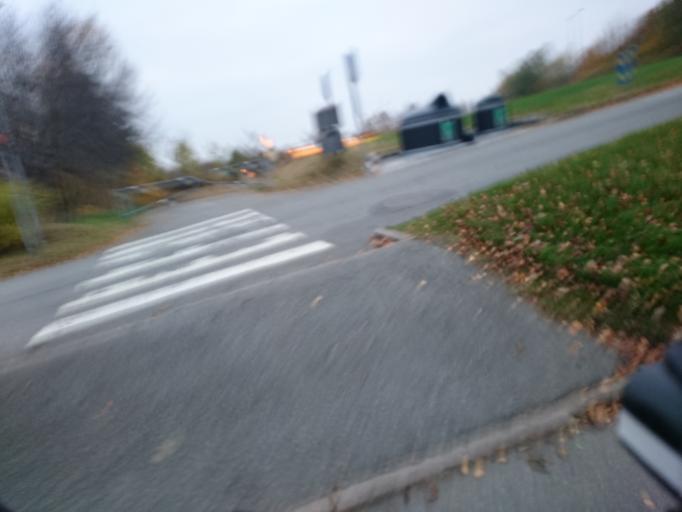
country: SE
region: Vaestra Goetaland
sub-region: Lerums Kommun
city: Lerum
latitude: 57.7516
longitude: 12.2500
